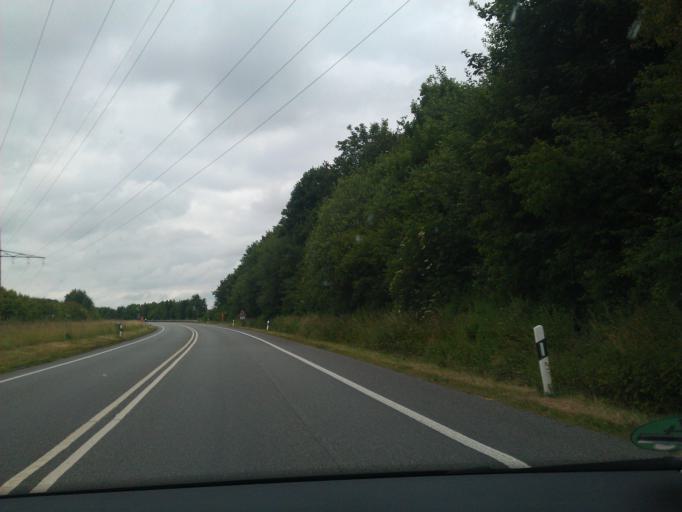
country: DE
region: Rheinland-Pfalz
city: Weselberg
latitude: 49.3174
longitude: 7.6174
